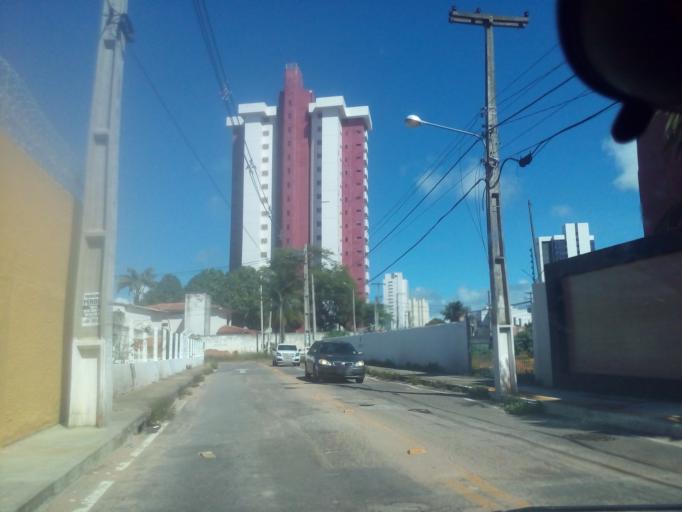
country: BR
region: Rio Grande do Norte
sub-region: Natal
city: Natal
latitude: -5.8536
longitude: -35.2045
